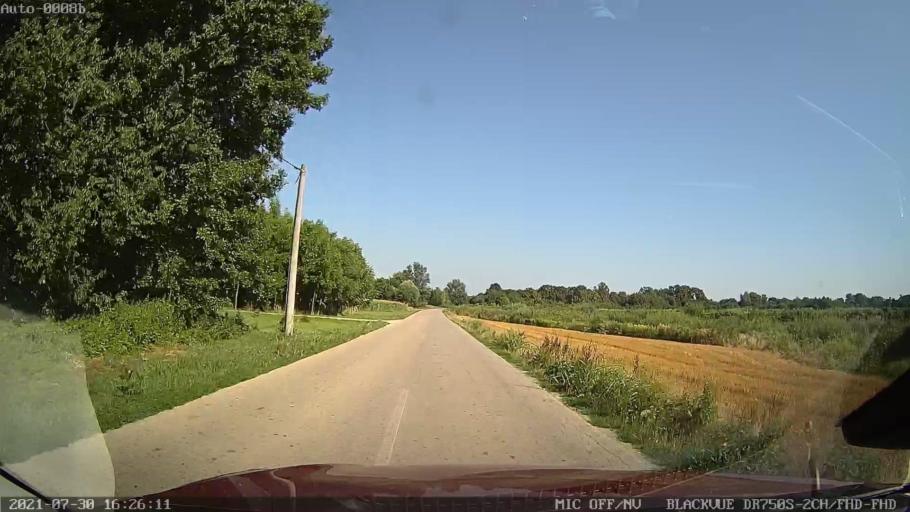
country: HR
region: Medimurska
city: Kursanec
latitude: 46.2793
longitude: 16.4198
